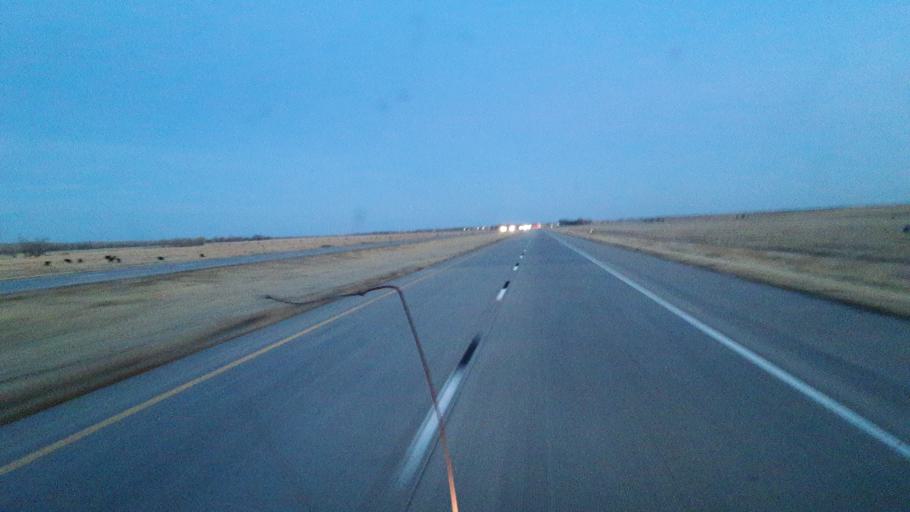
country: US
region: Nebraska
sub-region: Keith County
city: Ogallala
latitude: 41.1113
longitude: -101.5149
